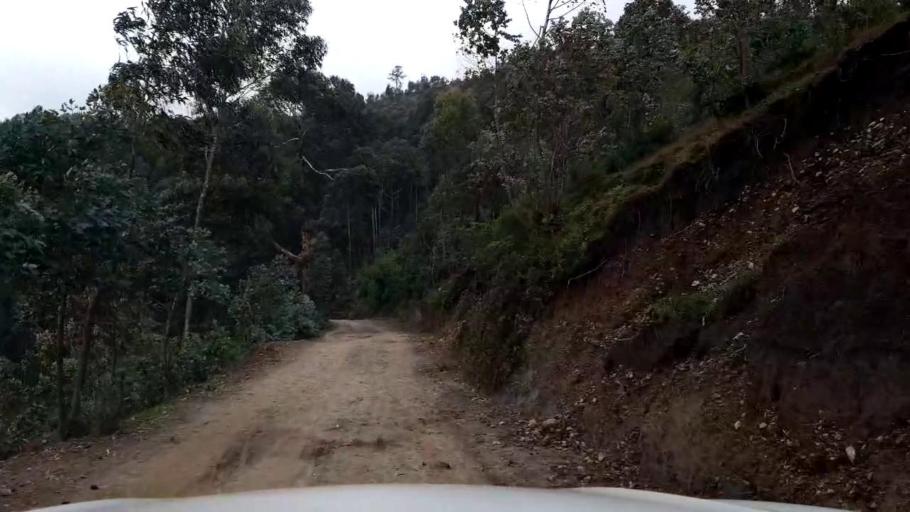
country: RW
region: Western Province
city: Kibuye
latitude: -1.9558
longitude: 29.4746
